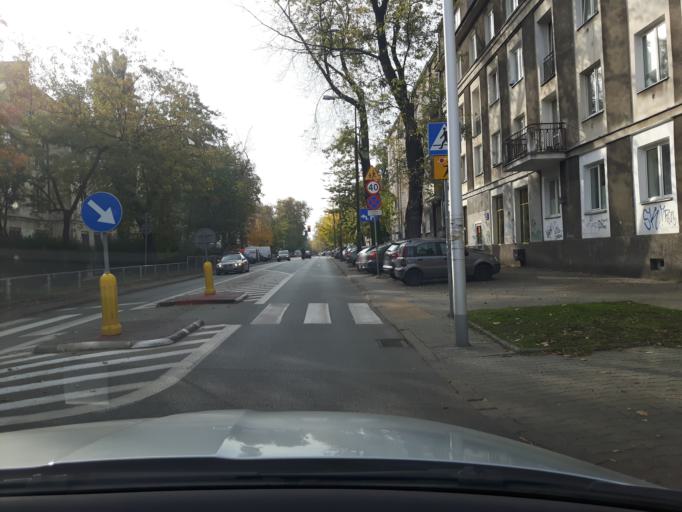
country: PL
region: Masovian Voivodeship
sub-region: Warszawa
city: Mokotow
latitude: 52.2001
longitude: 21.0176
